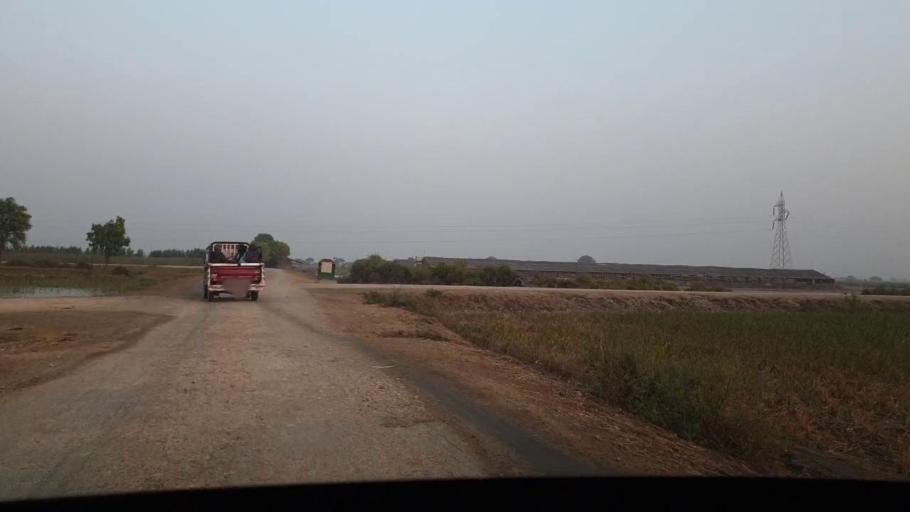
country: PK
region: Sindh
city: Chuhar Jamali
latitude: 24.4637
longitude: 68.0319
